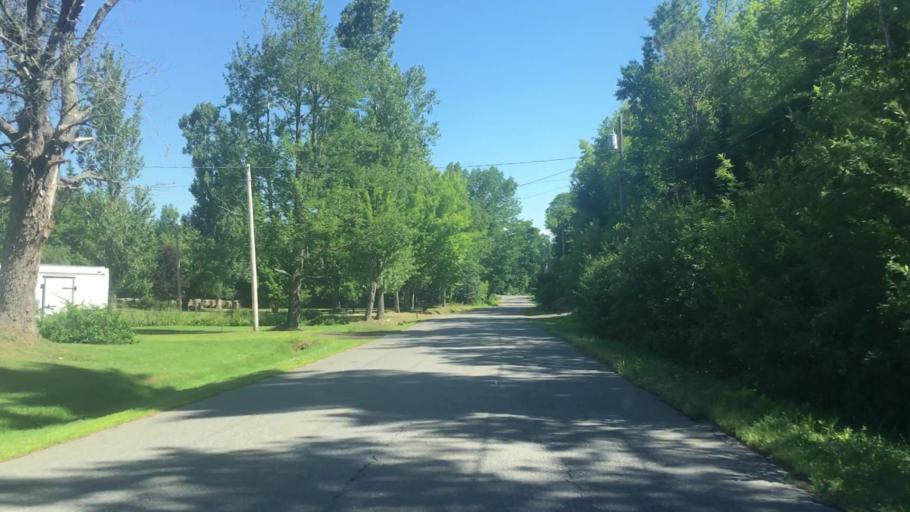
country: US
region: Maine
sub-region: Waldo County
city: Northport
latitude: 44.3800
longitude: -68.9814
